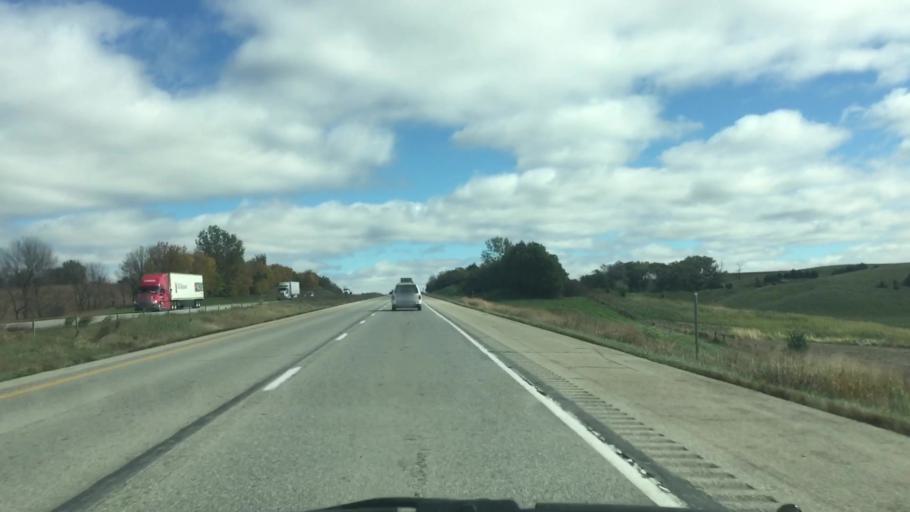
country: US
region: Iowa
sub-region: Poweshiek County
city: Grinnell
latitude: 41.6950
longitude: -92.8412
